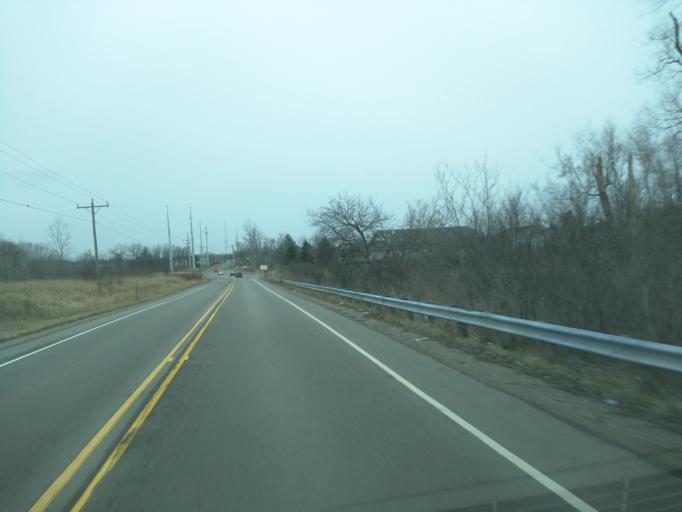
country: US
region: Michigan
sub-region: Eaton County
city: Waverly
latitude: 42.7151
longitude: -84.6229
